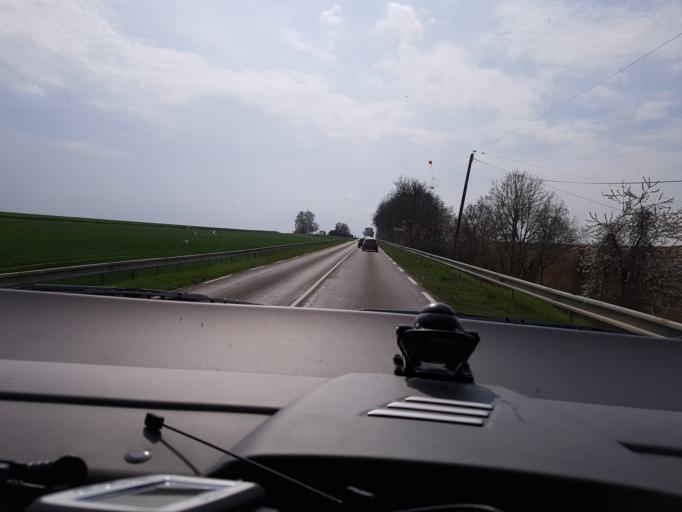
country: FR
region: Picardie
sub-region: Departement de l'Aisne
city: Coucy-le-Chateau-Auffrique
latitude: 49.4693
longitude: 3.3479
